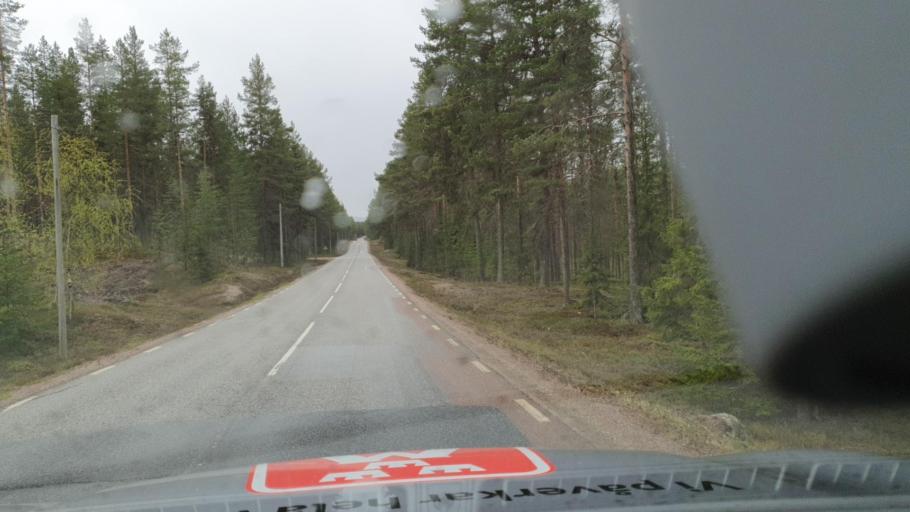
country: SE
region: Vaesternorrland
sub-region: Solleftea Kommun
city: As
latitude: 63.6924
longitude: 17.0242
